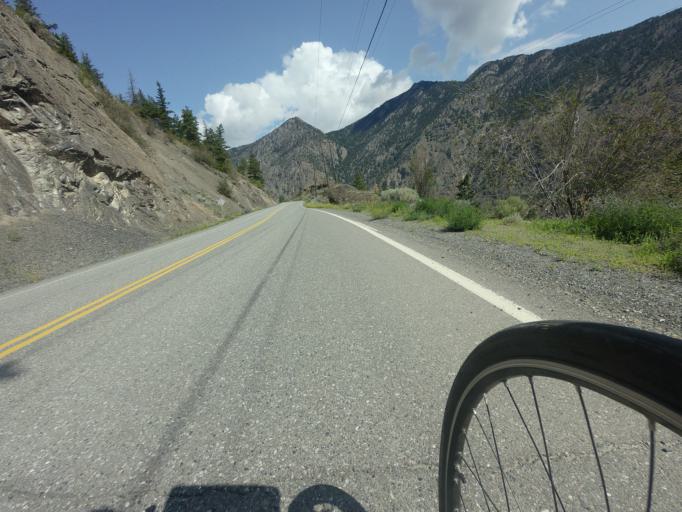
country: CA
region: British Columbia
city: Lillooet
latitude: 50.7516
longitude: -121.8933
